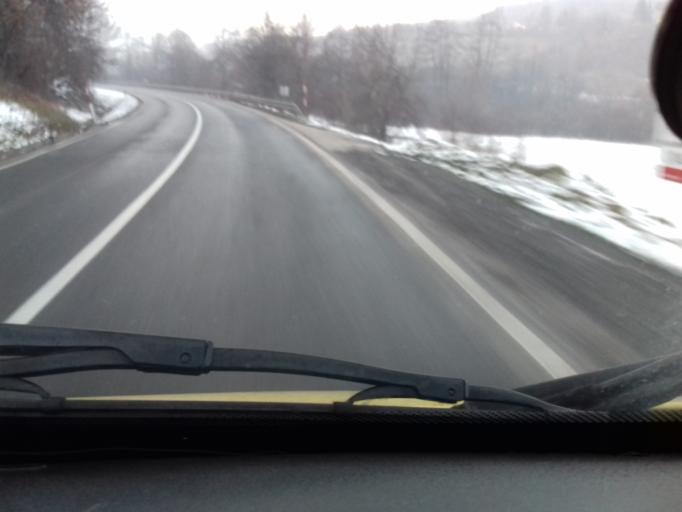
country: BA
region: Federation of Bosnia and Herzegovina
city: Vogosca
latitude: 43.8900
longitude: 18.3266
